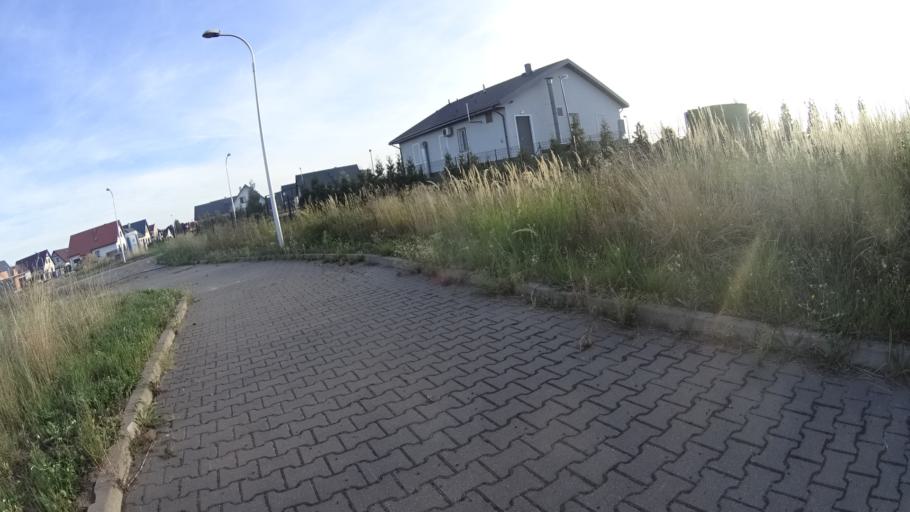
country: PL
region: Masovian Voivodeship
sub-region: Powiat warszawski zachodni
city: Ozarow Mazowiecki
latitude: 52.2345
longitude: 20.7720
